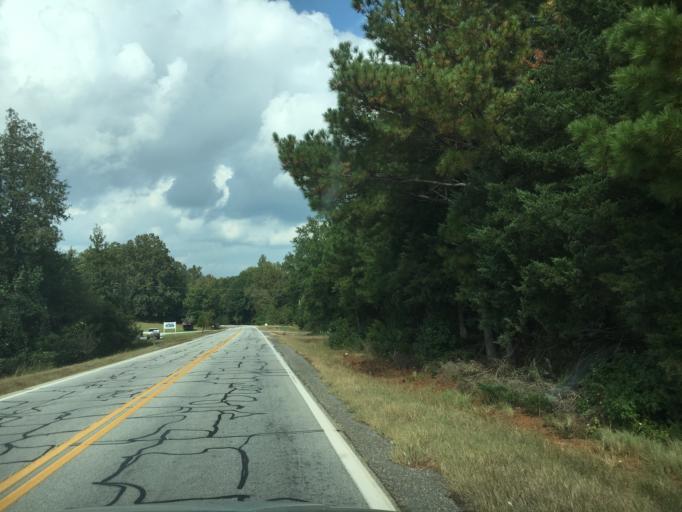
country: US
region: Georgia
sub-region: Elbert County
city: Elberton
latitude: 34.2159
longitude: -82.8922
